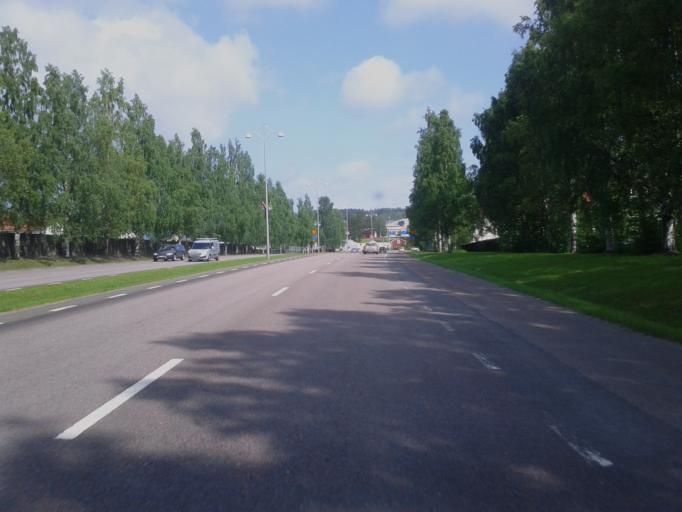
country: SE
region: Vaesterbotten
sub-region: Skelleftea Kommun
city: Skelleftea
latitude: 64.7555
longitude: 20.9627
